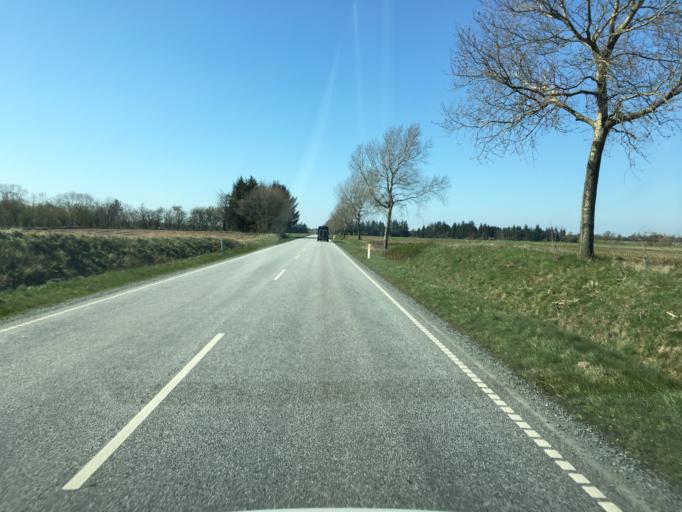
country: DK
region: South Denmark
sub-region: Aabenraa Kommune
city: Tinglev
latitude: 54.9464
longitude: 9.3527
